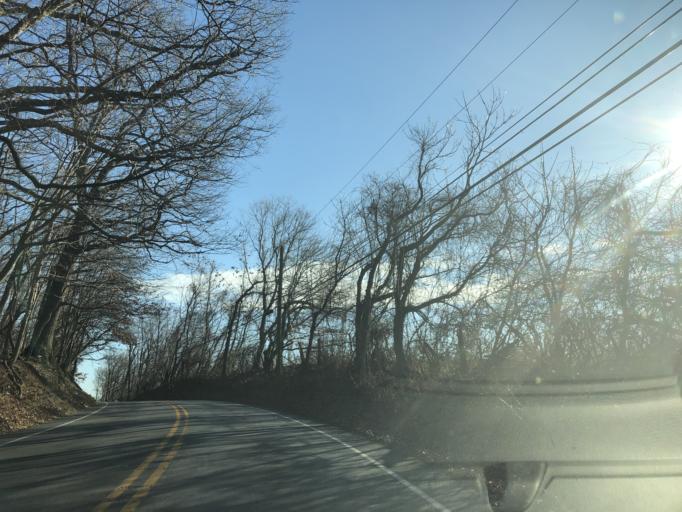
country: US
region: Pennsylvania
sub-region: Chester County
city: South Coatesville
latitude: 39.9259
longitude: -75.8275
